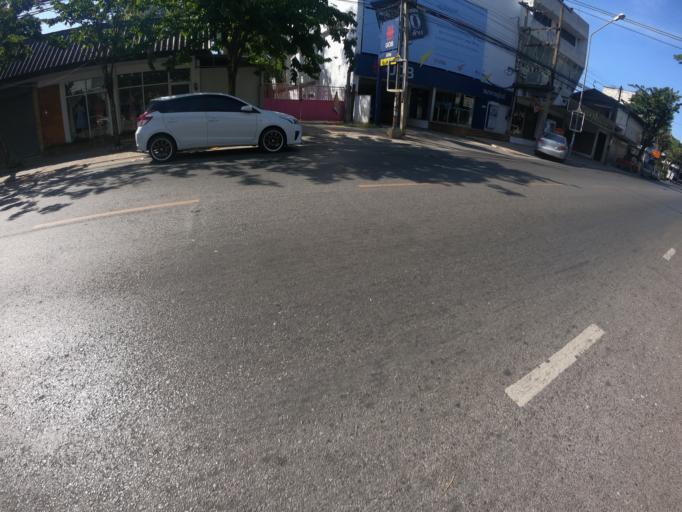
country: TH
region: Khon Kaen
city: Khon Kaen
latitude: 16.4358
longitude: 102.8345
